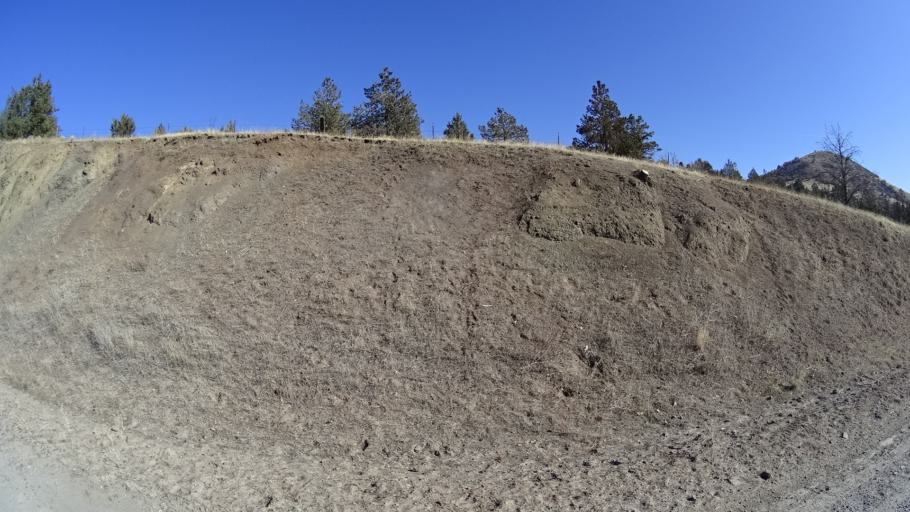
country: US
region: California
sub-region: Siskiyou County
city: Montague
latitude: 41.8055
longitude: -122.3711
